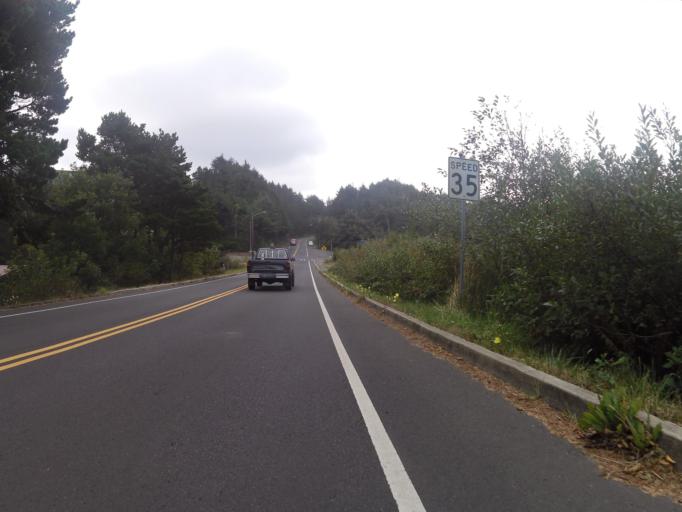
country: US
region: Oregon
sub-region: Lincoln County
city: Newport
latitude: 44.6598
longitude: -124.0554
